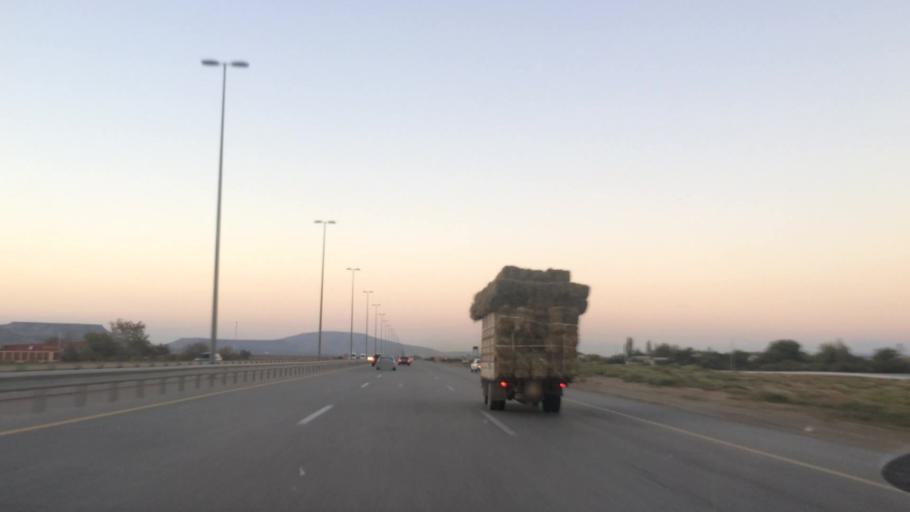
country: AZ
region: Baki
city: Qobustan
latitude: 40.0201
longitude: 49.4252
